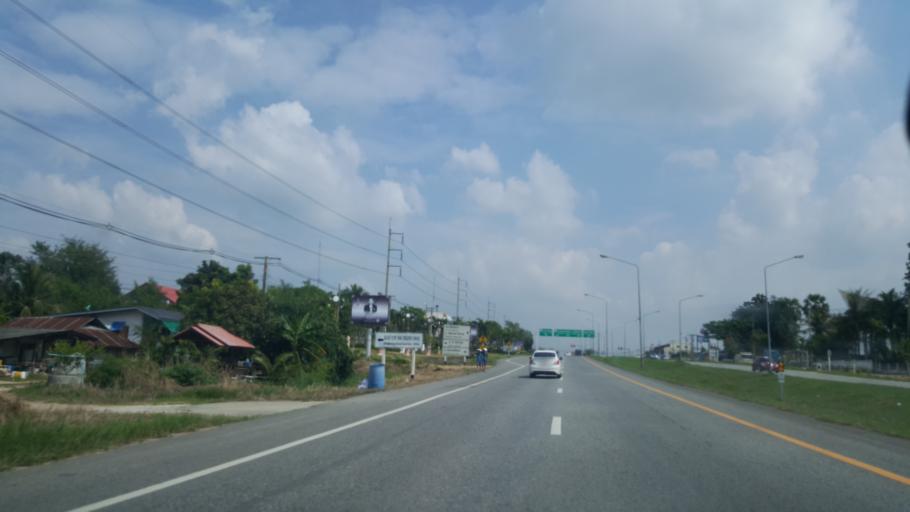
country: TH
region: Chon Buri
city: Ban Talat Bueng
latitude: 12.9495
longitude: 101.0456
